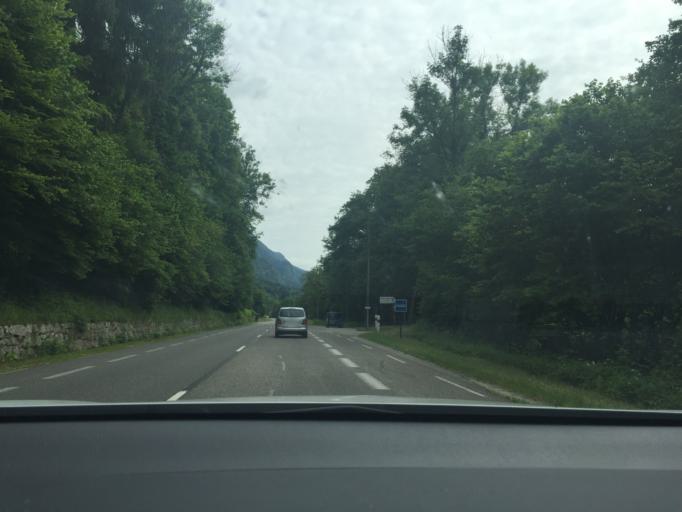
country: FR
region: Rhone-Alpes
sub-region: Departement de la Savoie
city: Vimines
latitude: 45.5142
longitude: 5.8517
